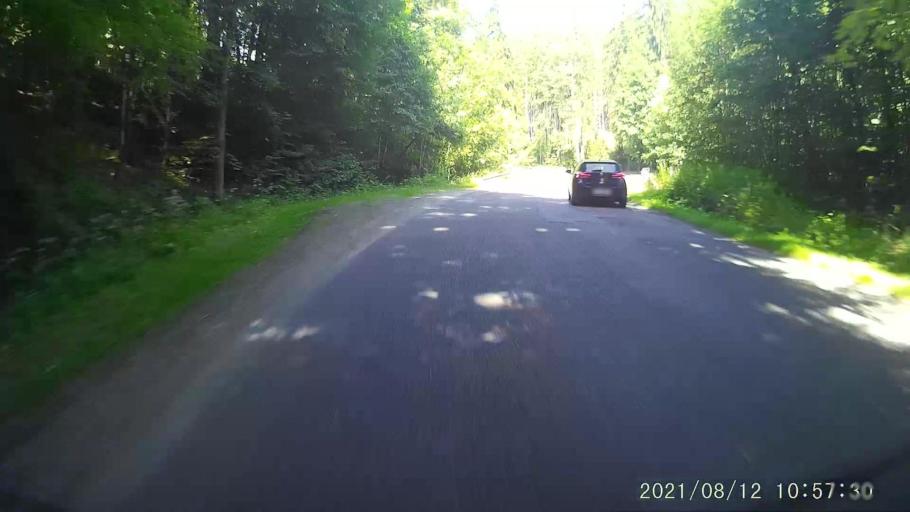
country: PL
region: Lower Silesian Voivodeship
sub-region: Powiat klodzki
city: Polanica-Zdroj
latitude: 50.3982
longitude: 16.4958
